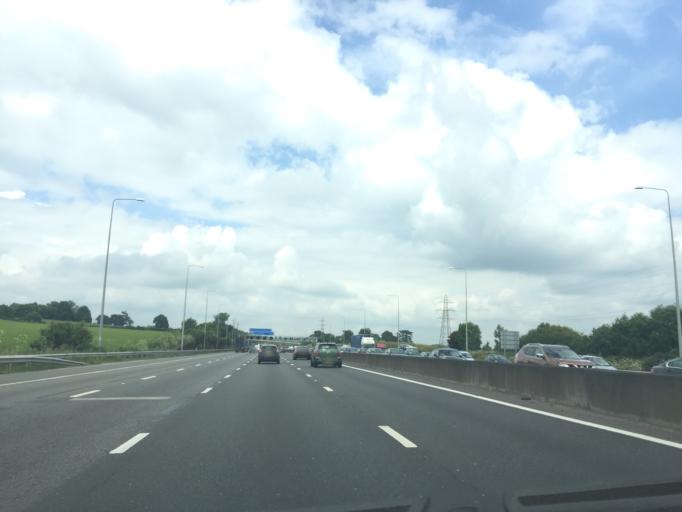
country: GB
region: England
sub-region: Buckinghamshire
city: Chalfont Saint Peter
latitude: 51.6157
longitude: -0.5264
